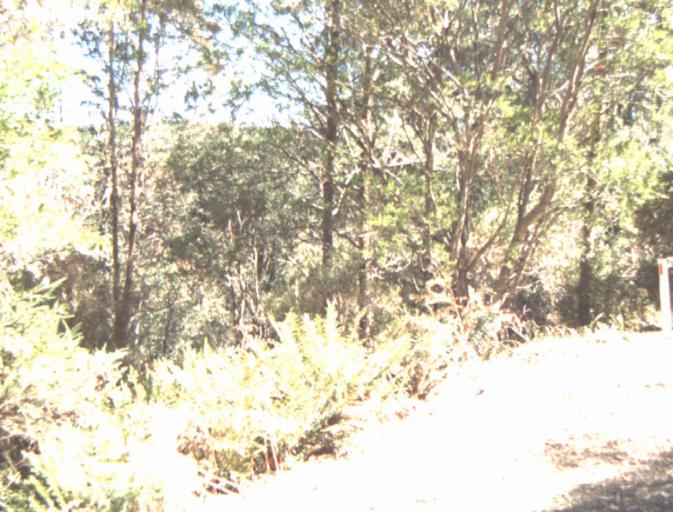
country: AU
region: Tasmania
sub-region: Dorset
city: Scottsdale
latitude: -41.2844
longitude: 147.3395
